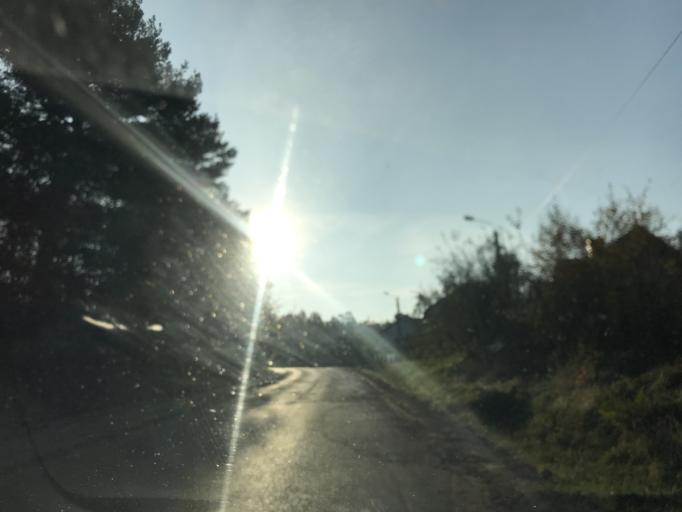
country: PL
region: Pomeranian Voivodeship
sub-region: Powiat pucki
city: Krokowa
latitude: 54.7992
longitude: 18.1106
